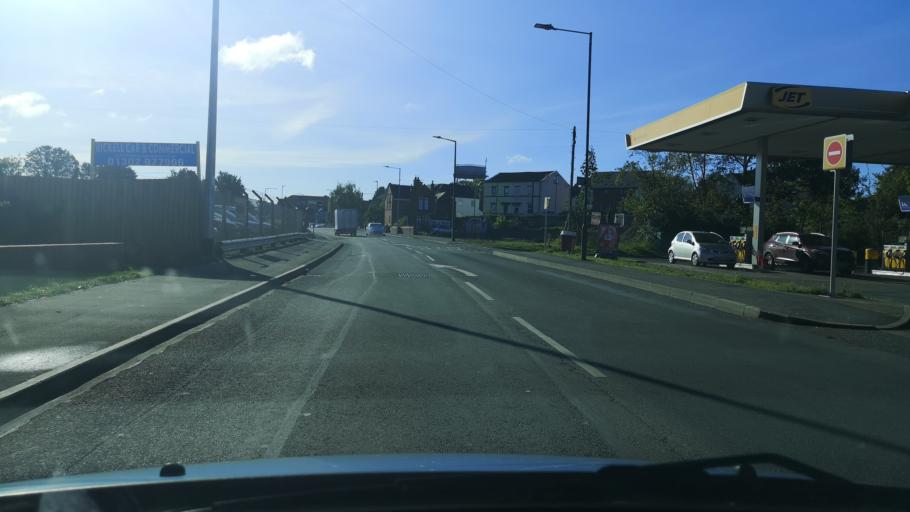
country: GB
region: England
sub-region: Doncaster
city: Askern
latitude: 53.6195
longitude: -1.1535
